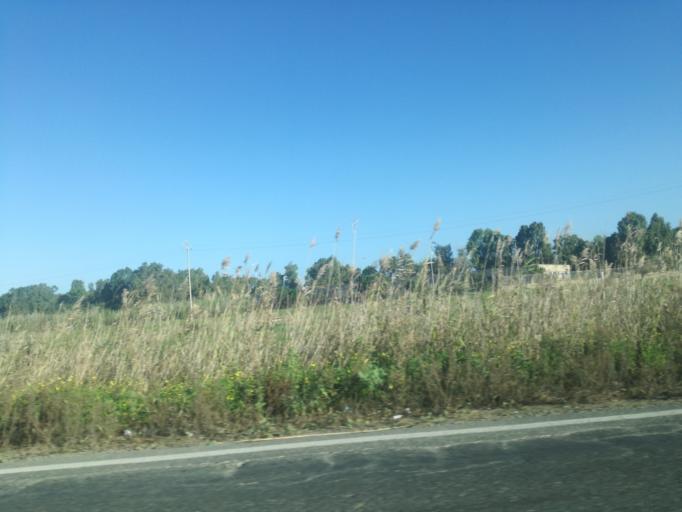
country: IT
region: Sicily
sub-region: Provincia di Caltanissetta
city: Gela
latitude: 37.0569
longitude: 14.2922
